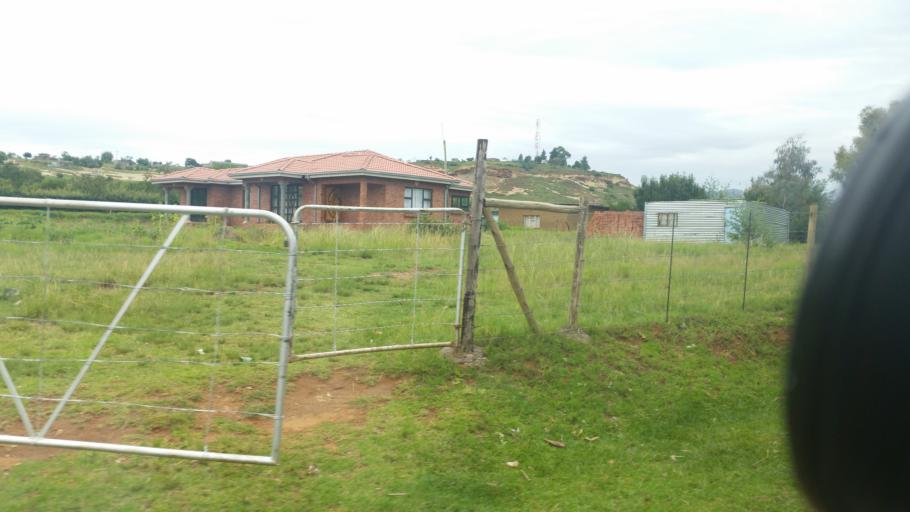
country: LS
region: Berea
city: Teyateyaneng
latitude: -29.1181
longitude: 27.9665
